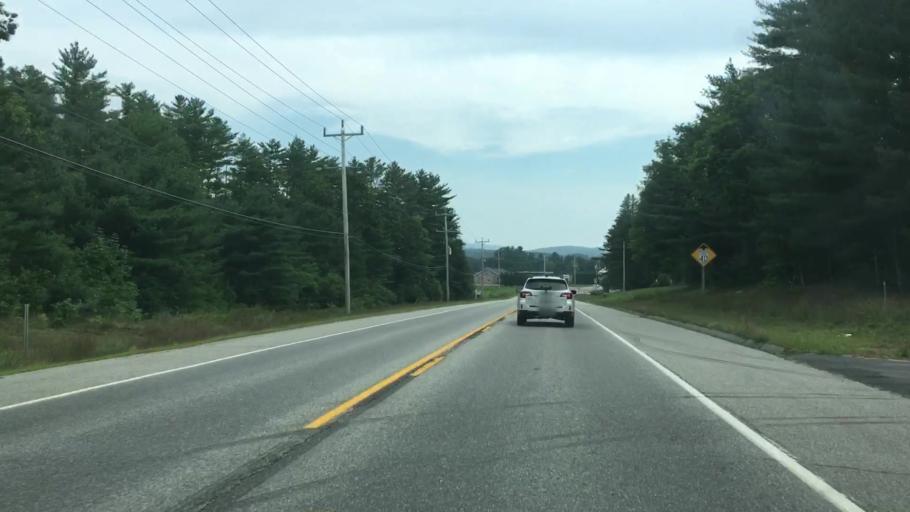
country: US
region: Maine
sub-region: Oxford County
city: Bethel
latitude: 44.4284
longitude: -70.7990
